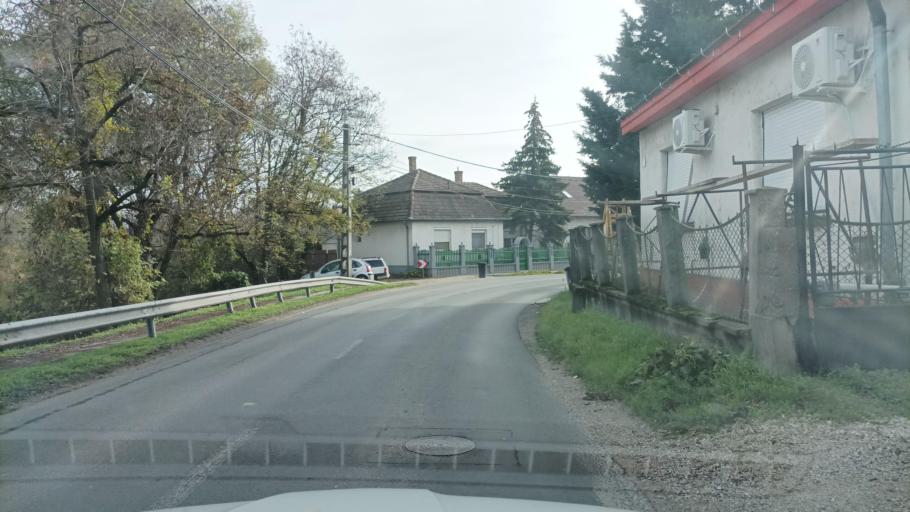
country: HU
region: Pest
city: Rackeve
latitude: 47.1375
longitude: 18.9479
